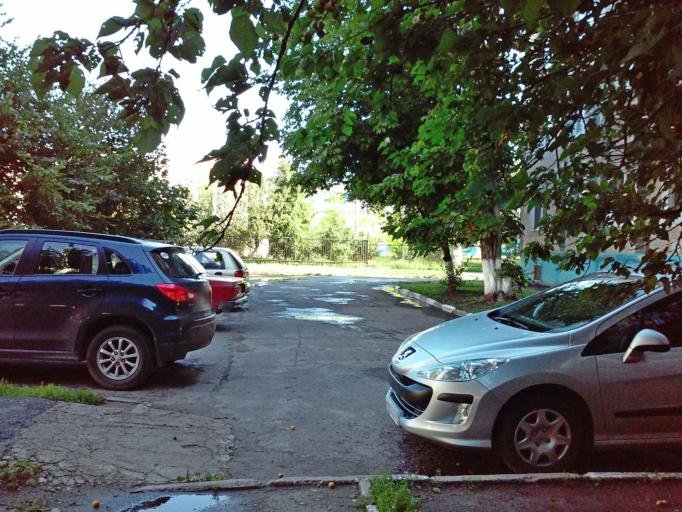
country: RU
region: Belgorod
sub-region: Belgorodskiy Rayon
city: Belgorod
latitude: 50.5625
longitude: 36.5672
